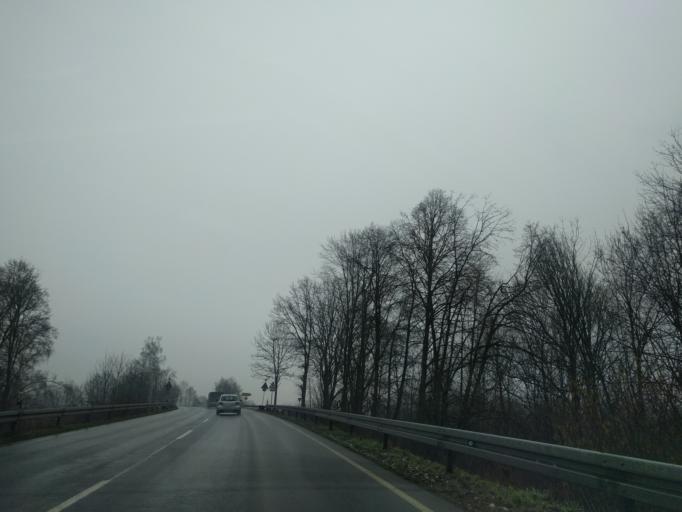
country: DE
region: Bavaria
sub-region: Lower Bavaria
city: Aholming
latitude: 48.7471
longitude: 12.9271
